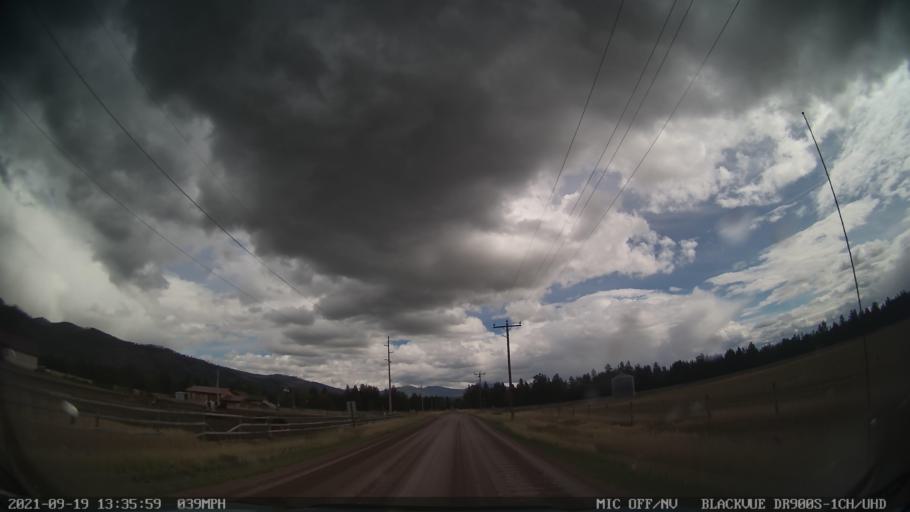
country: US
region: Montana
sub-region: Missoula County
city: Seeley Lake
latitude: 47.1065
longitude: -113.3042
